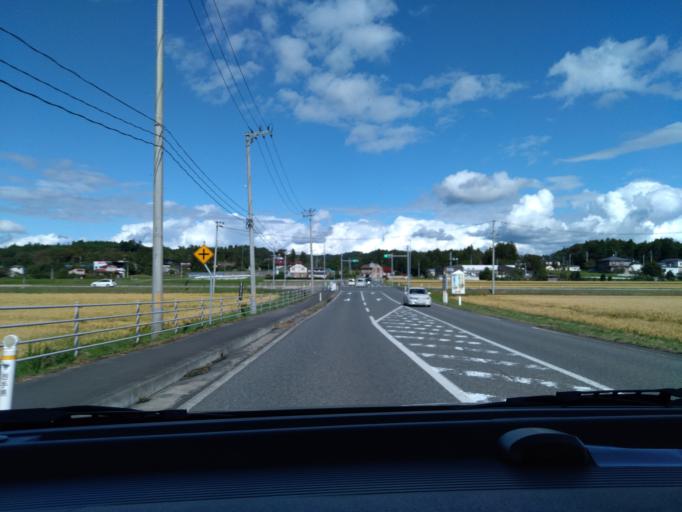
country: JP
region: Iwate
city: Ichinoseki
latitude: 38.8304
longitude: 141.1913
